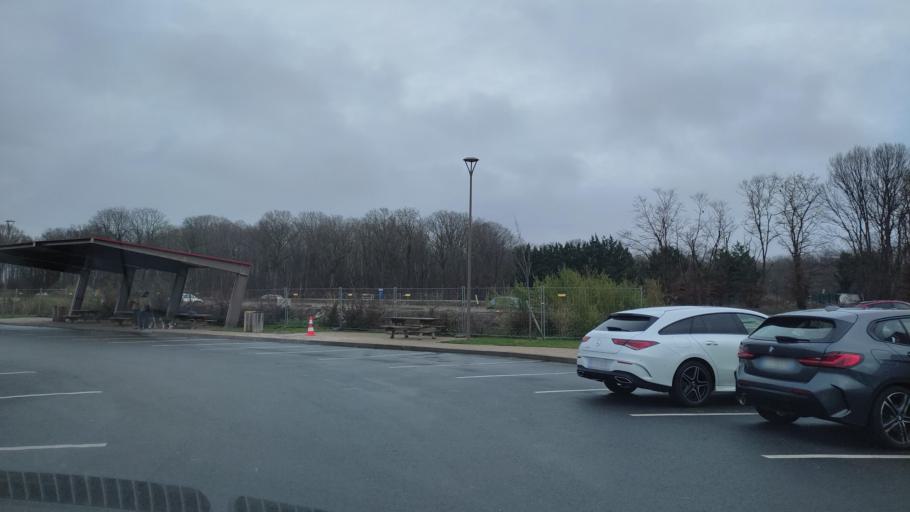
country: FR
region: Centre
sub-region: Departement du Loiret
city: Gidy
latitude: 47.9772
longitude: 1.8584
